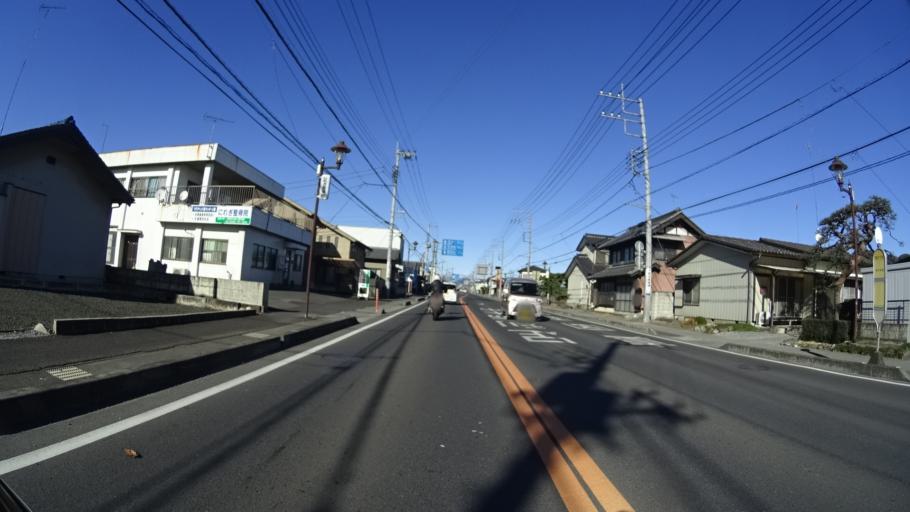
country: JP
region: Tochigi
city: Kanuma
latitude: 36.5041
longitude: 139.7512
